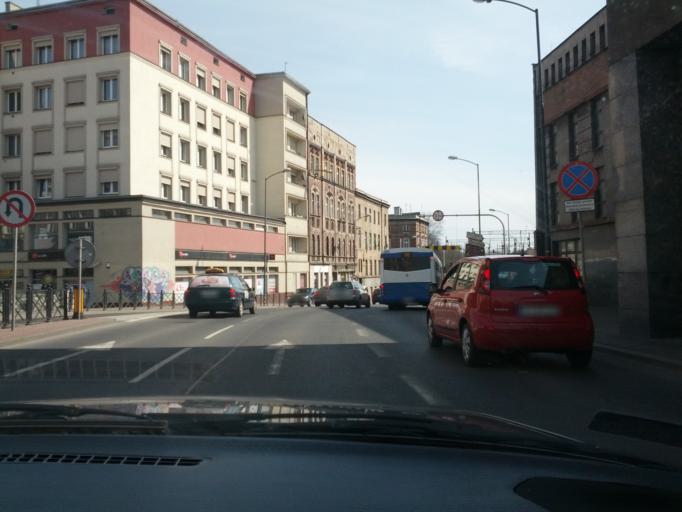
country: PL
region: Silesian Voivodeship
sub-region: Bytom
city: Bytom
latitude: 50.3434
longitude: 18.9154
